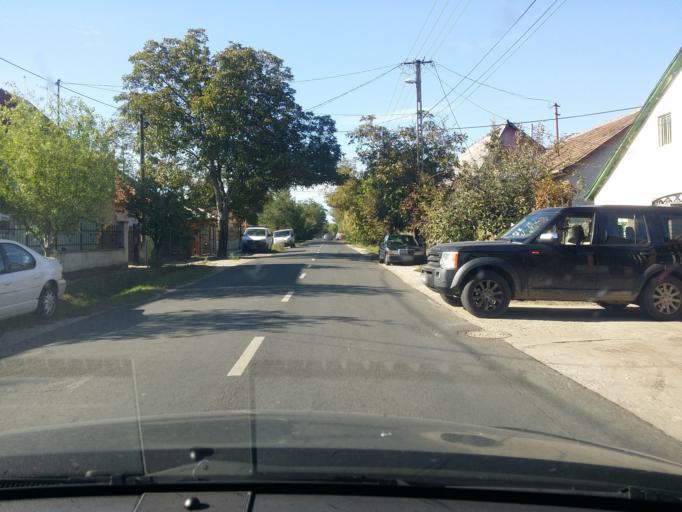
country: HU
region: Pest
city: God
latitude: 47.7009
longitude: 19.1501
